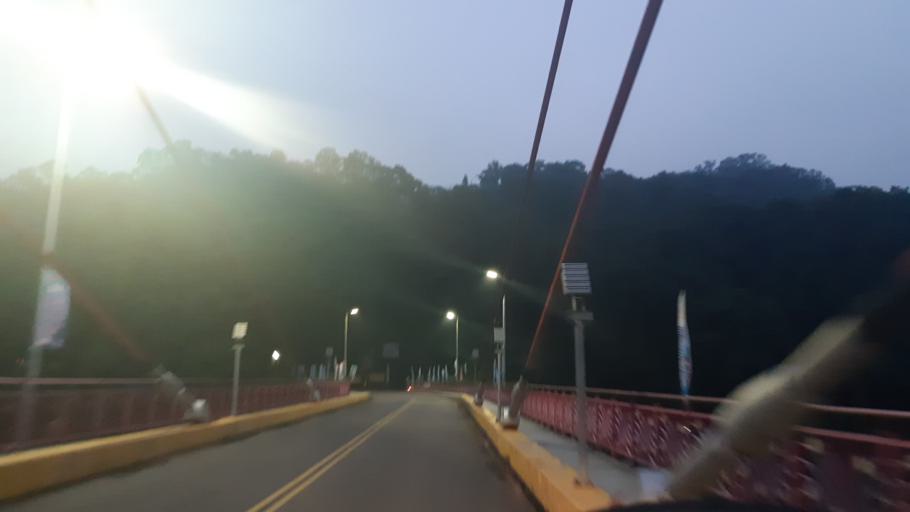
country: TW
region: Taiwan
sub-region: Hsinchu
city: Zhubei
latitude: 24.7060
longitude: 121.1483
